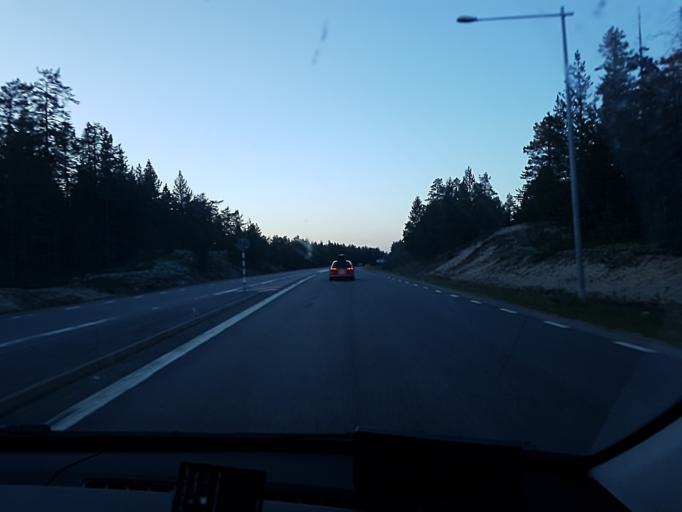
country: SE
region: Norrbotten
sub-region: Lulea Kommun
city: Bergnaset
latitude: 65.5745
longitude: 22.0731
